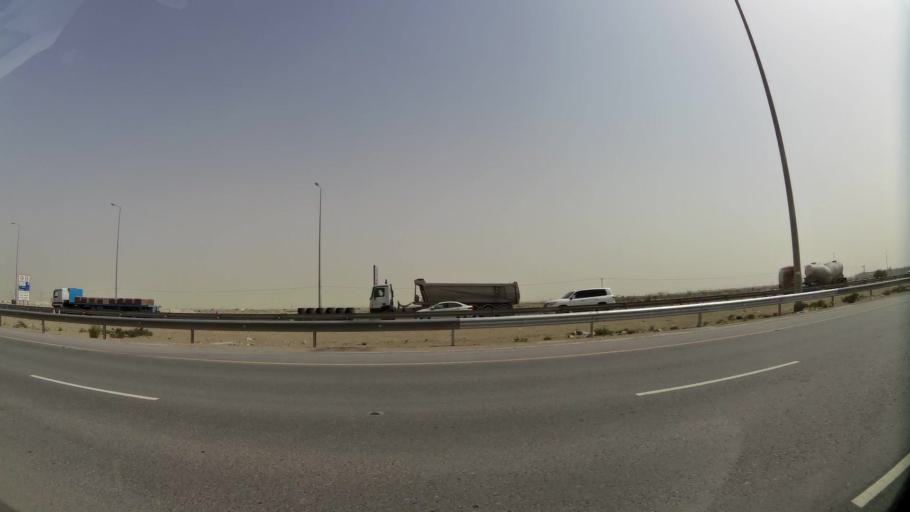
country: QA
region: Baladiyat ar Rayyan
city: Ar Rayyan
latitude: 25.1687
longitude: 51.3160
